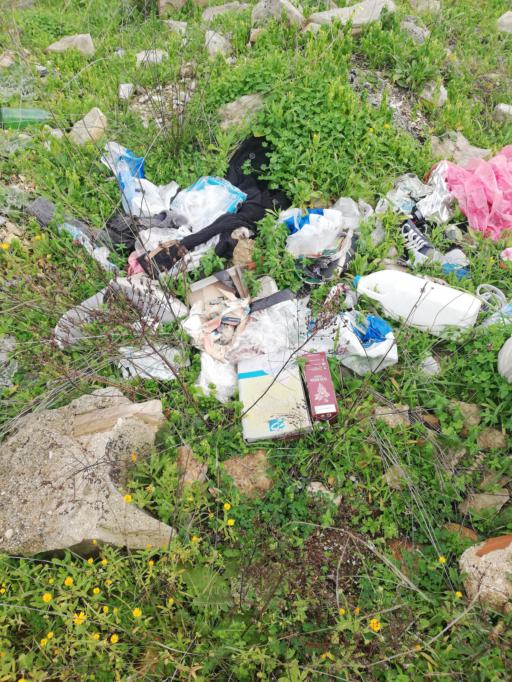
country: IT
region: Apulia
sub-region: Provincia di Bari
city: Palo del Colle
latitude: 41.0699
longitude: 16.6814
